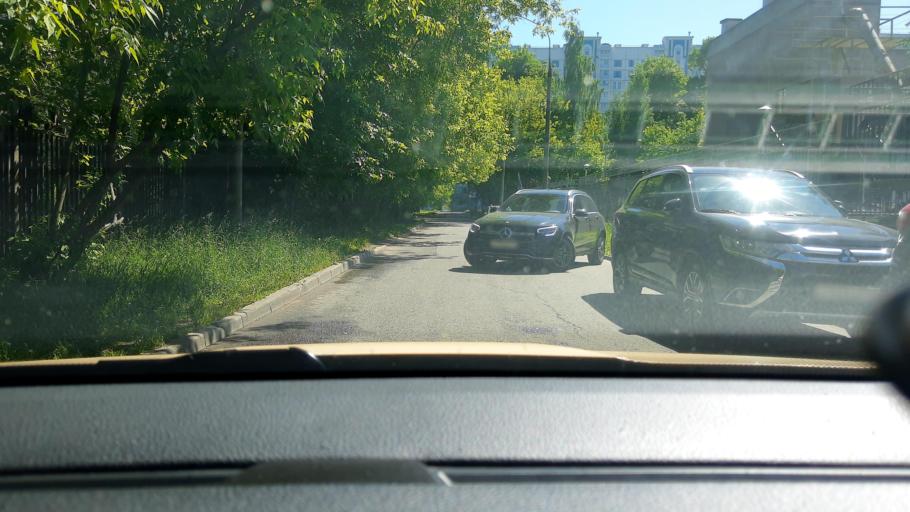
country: RU
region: Moscow
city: Yaroslavskiy
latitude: 55.8885
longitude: 37.7064
